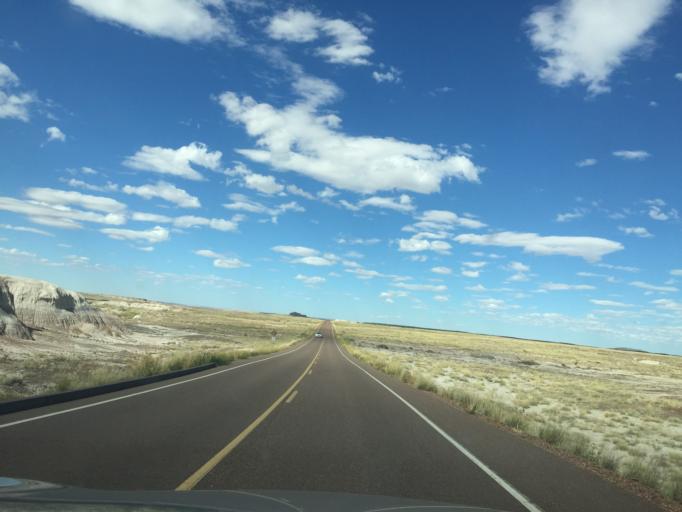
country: US
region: Arizona
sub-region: Navajo County
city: Holbrook
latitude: 34.8469
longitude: -109.8024
